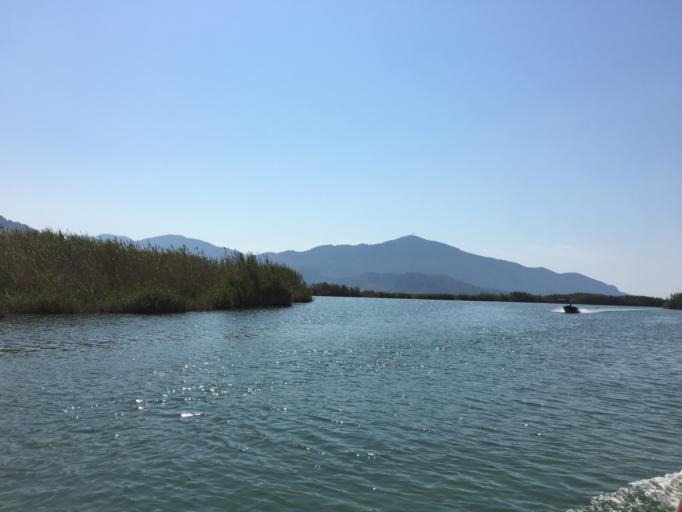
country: TR
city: Dalyan
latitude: 36.8167
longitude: 28.6340
